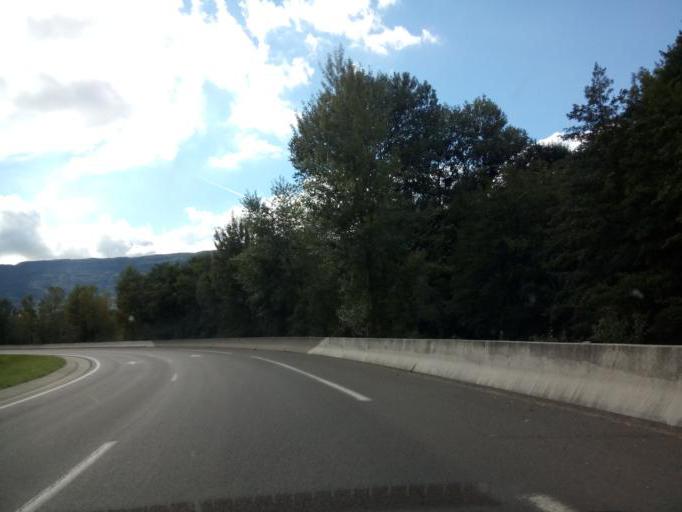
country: FR
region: Rhone-Alpes
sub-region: Departement de la Savoie
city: La Motte-Servolex
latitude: 45.6062
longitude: 5.8844
